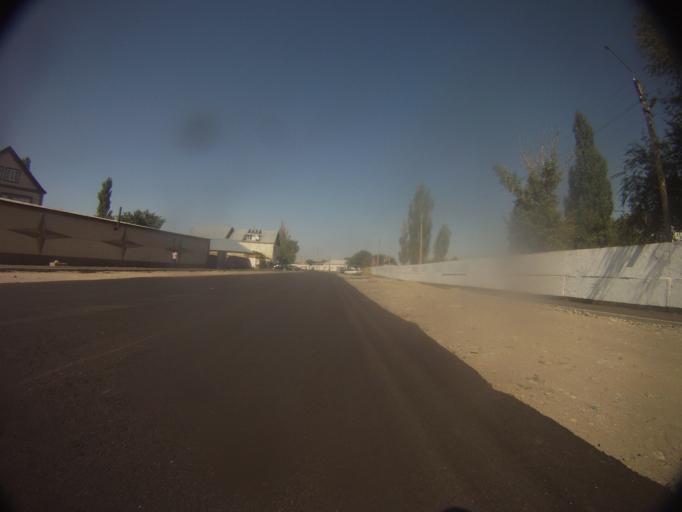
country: KZ
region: Zhambyl
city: Taraz
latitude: 42.8947
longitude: 71.3933
